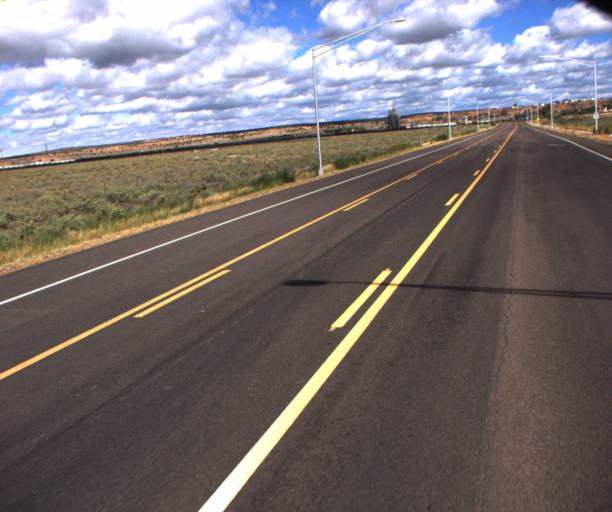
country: US
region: Arizona
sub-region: Apache County
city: Houck
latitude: 35.1990
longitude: -109.3327
